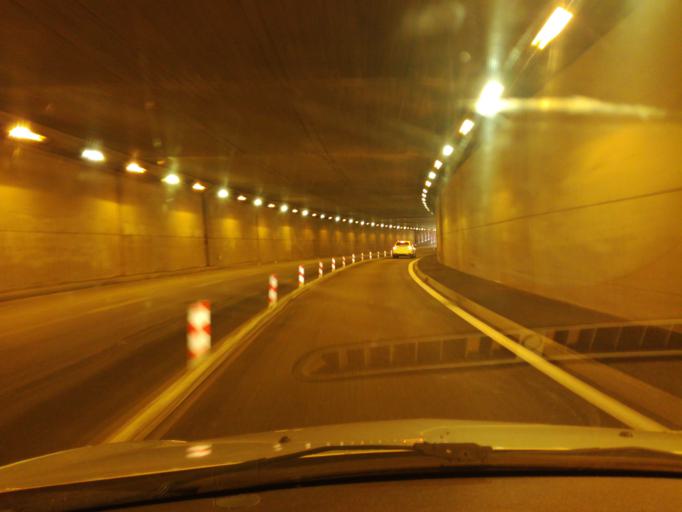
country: FR
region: Provence-Alpes-Cote d'Azur
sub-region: Departement des Alpes-Maritimes
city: Grasse
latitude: 43.6383
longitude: 6.9371
